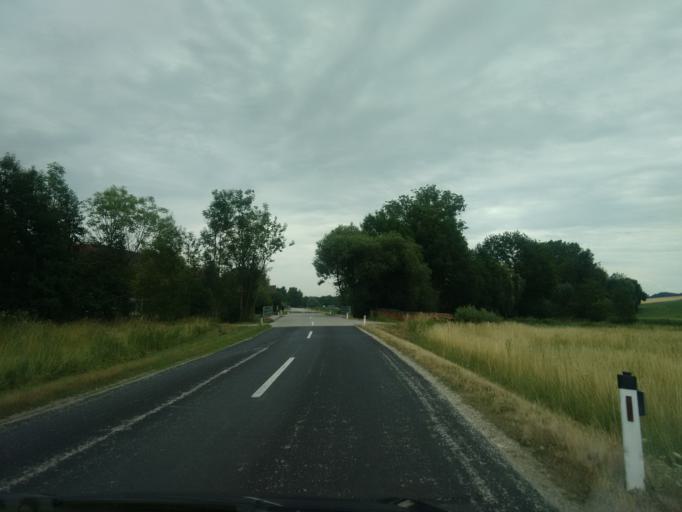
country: AT
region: Upper Austria
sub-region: Politischer Bezirk Grieskirchen
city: Bad Schallerbach
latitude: 48.1965
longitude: 13.8902
